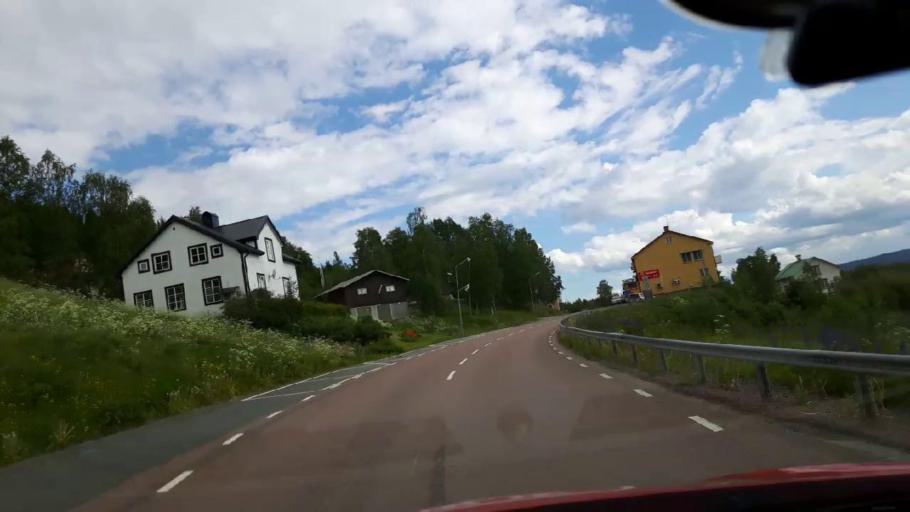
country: SE
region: Jaemtland
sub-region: Krokoms Kommun
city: Valla
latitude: 64.0681
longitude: 14.1397
